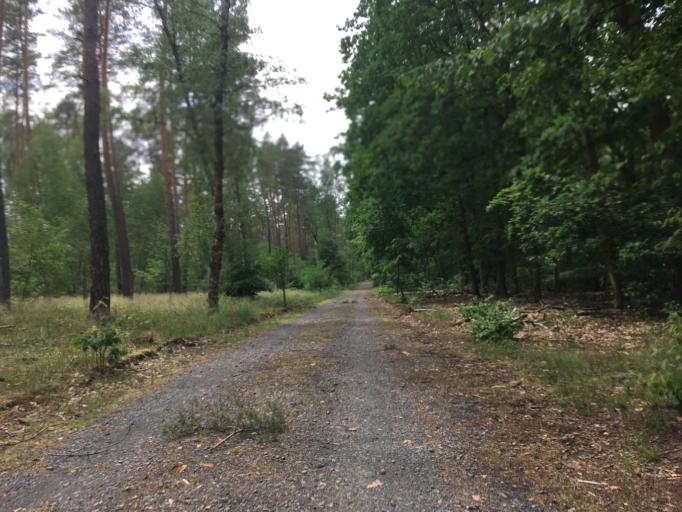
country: DE
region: Berlin
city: Muggelheim
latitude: 52.4126
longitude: 13.6842
